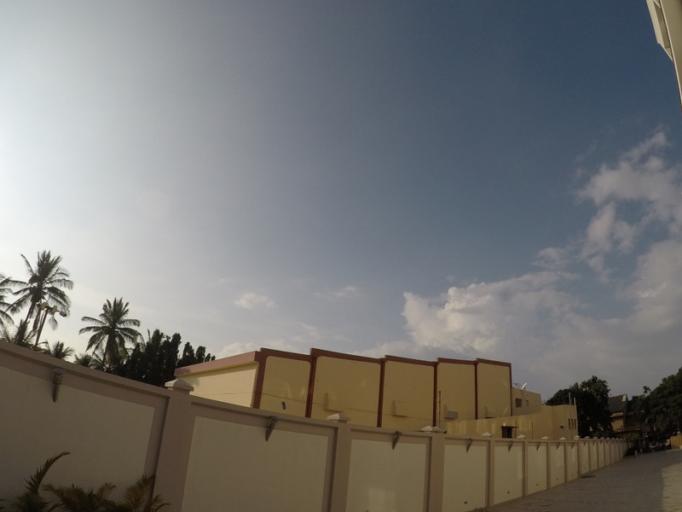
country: IN
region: Karnataka
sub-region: Chikmagalur
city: Chikmagalur
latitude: 13.3168
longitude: 75.7709
